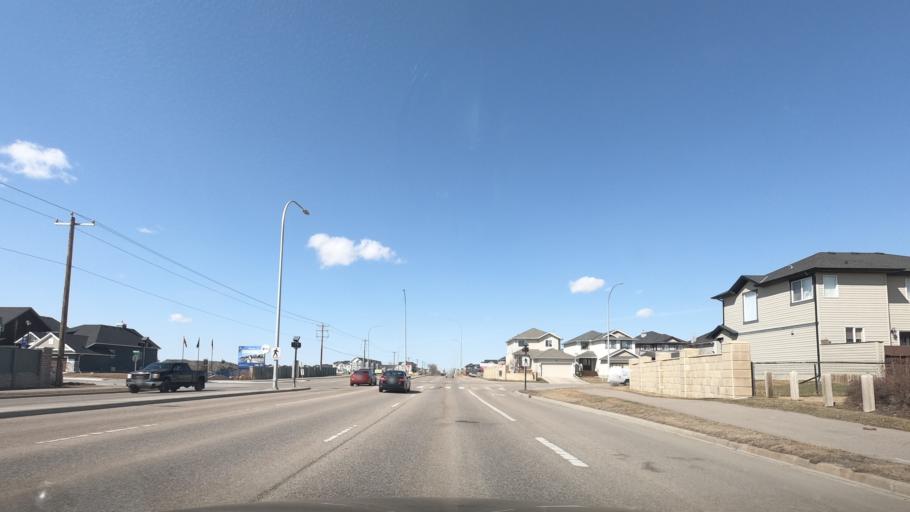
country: CA
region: Alberta
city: Airdrie
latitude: 51.2782
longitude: -114.0251
